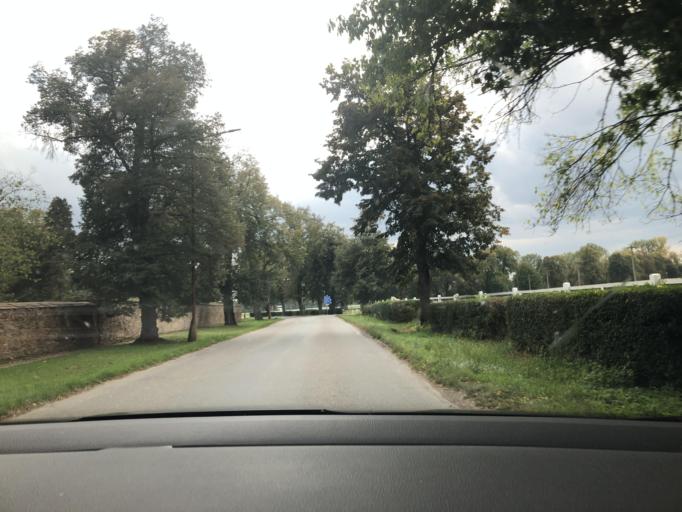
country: CZ
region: Pardubicky
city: Recany nad Labem
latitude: 50.0587
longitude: 15.4830
